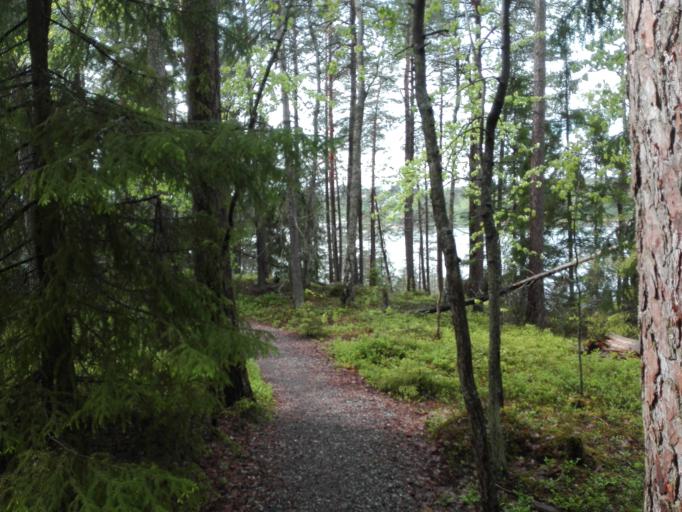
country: SE
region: Stockholm
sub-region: Nacka Kommun
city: Fisksatra
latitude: 59.2957
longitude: 18.2680
